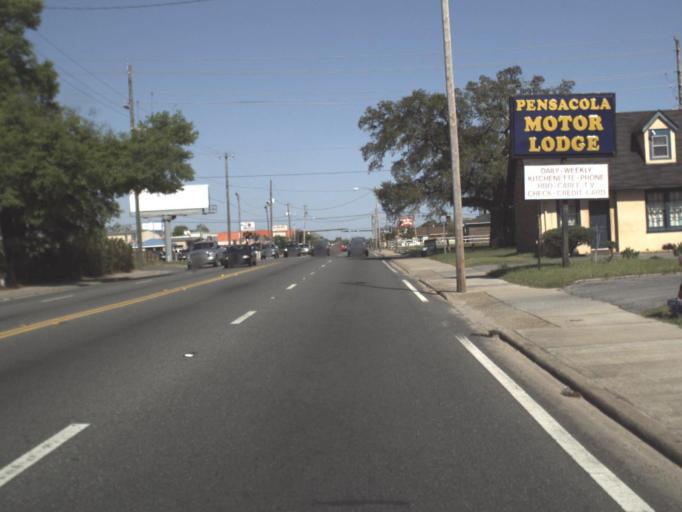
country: US
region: Florida
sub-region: Escambia County
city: Pensacola
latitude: 30.4208
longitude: -87.2443
